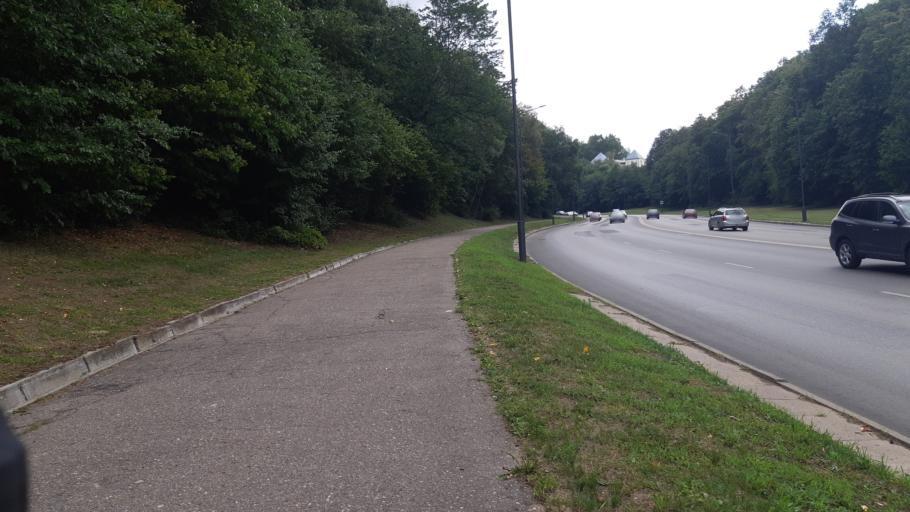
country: LT
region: Kauno apskritis
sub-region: Kaunas
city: Eiguliai
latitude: 54.9300
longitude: 23.9194
